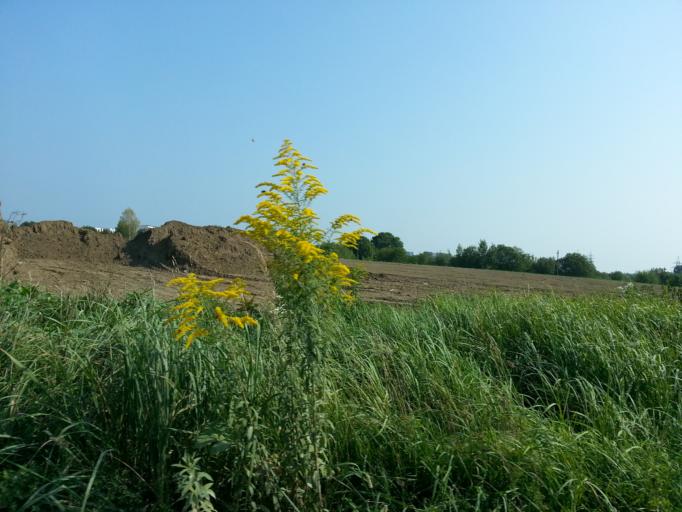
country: LT
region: Vilnius County
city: Pasilaiciai
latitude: 54.7277
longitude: 25.2060
